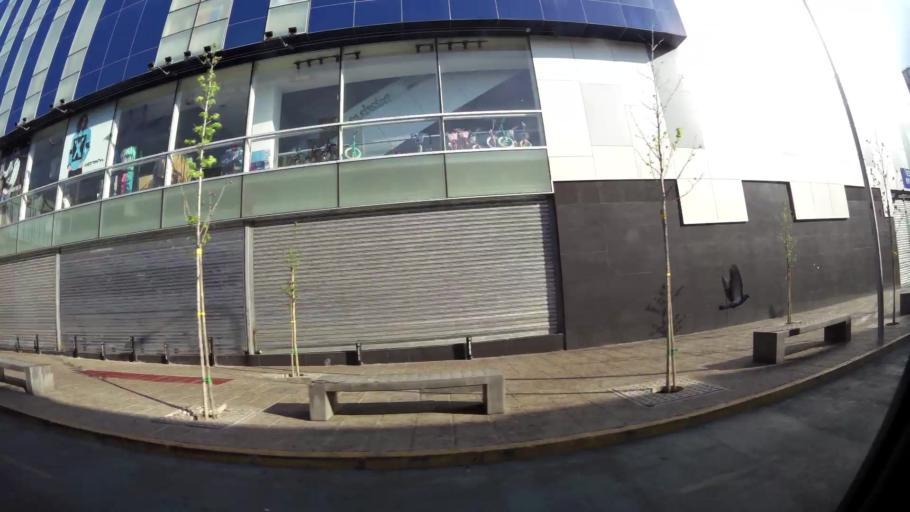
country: CL
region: Santiago Metropolitan
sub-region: Provincia de Santiago
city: Santiago
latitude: -33.4352
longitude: -70.6521
